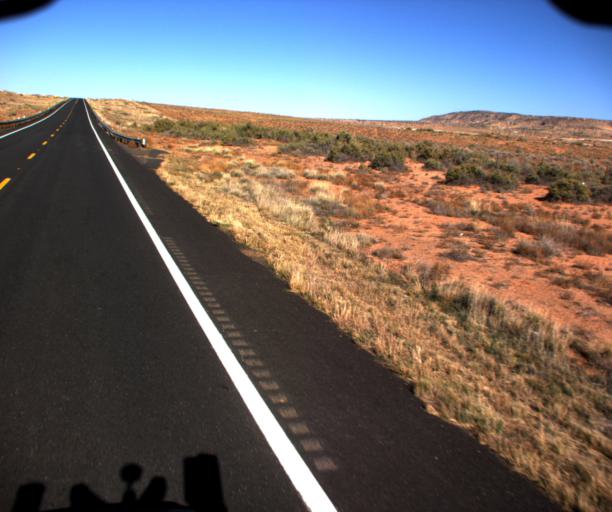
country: US
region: Arizona
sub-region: Coconino County
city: Kaibito
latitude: 36.3530
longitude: -110.9084
